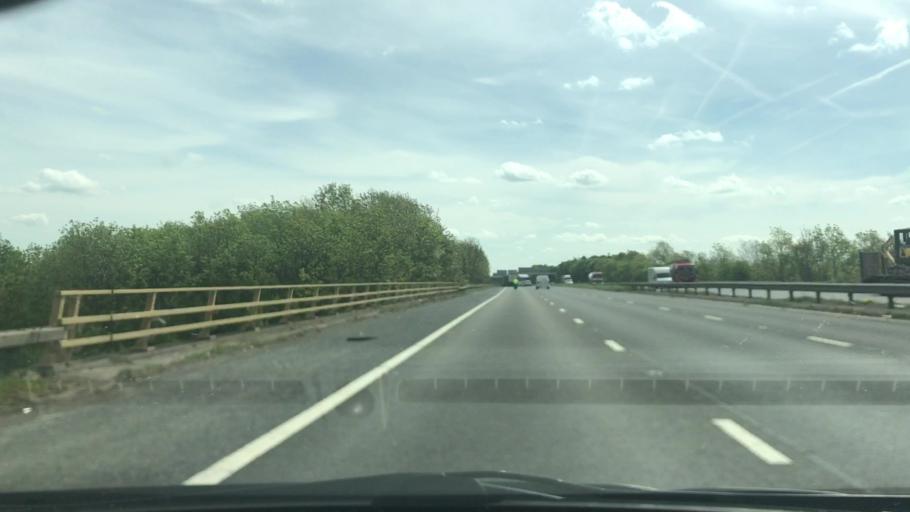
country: GB
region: England
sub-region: City and Borough of Wakefield
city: Knottingley
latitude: 53.6955
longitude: -1.2662
